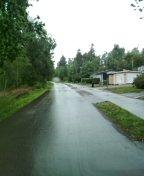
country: SE
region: Vaestmanland
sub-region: Kungsors Kommun
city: Kungsoer
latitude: 59.4807
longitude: 16.0590
